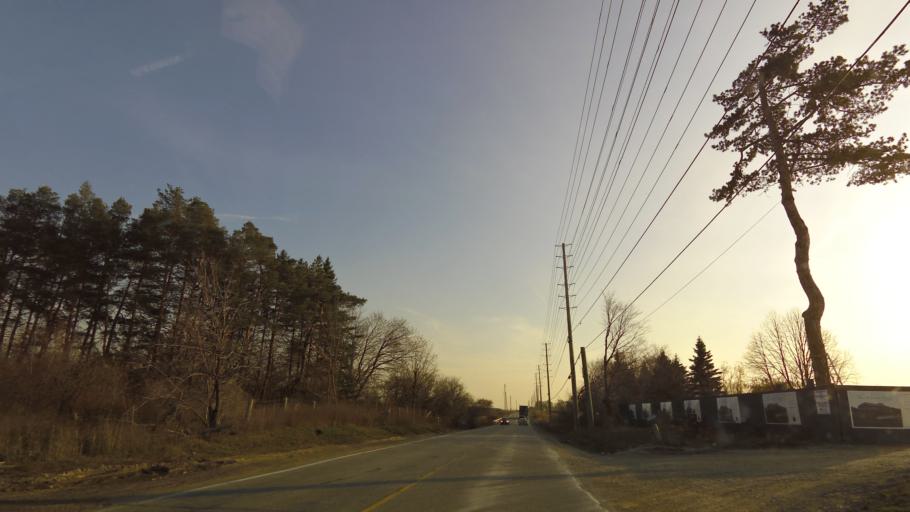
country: CA
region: Ontario
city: Vaughan
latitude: 43.7975
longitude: -79.6537
